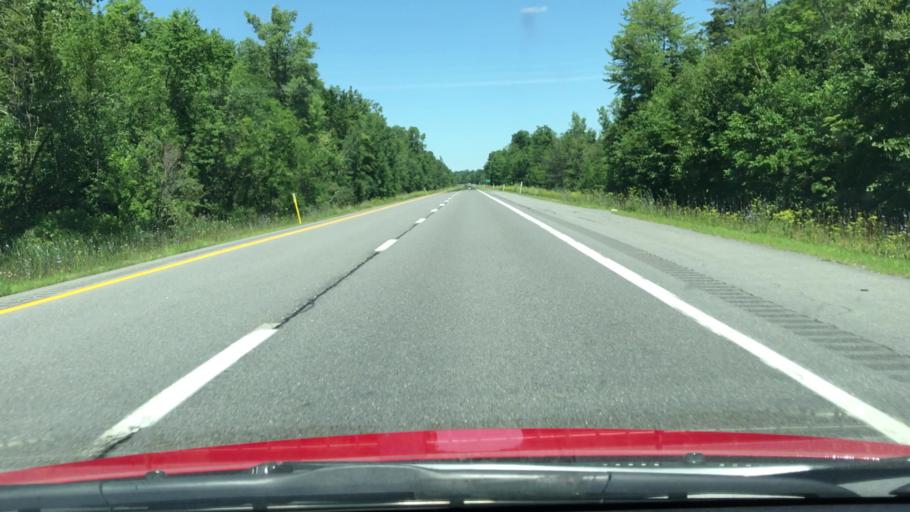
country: US
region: New York
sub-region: Clinton County
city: Champlain
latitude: 44.9041
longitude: -73.4530
